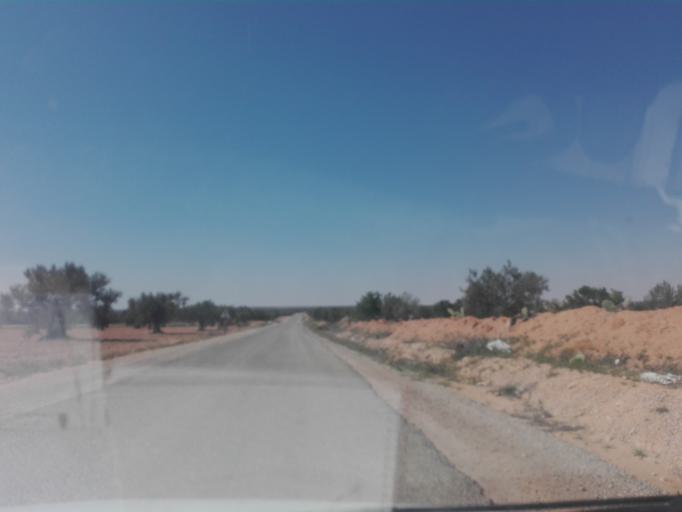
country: TN
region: Safaqis
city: Bi'r `Ali Bin Khalifah
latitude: 34.6686
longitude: 10.3466
